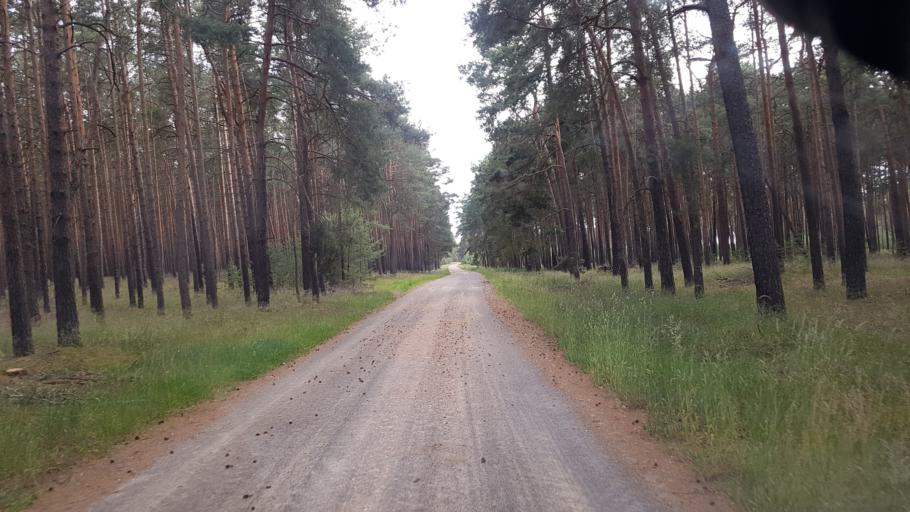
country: DE
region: Brandenburg
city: Herzberg
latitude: 51.7376
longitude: 13.2758
